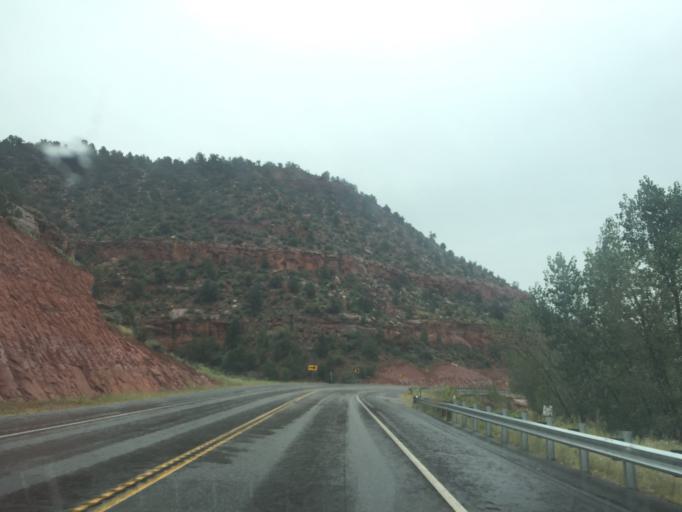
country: US
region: Utah
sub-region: Kane County
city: Kanab
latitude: 37.0751
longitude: -112.5367
